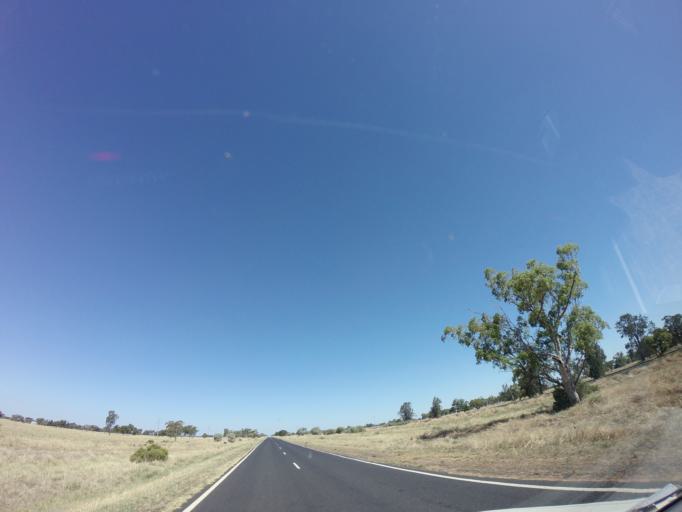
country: AU
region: New South Wales
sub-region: Bogan
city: Nyngan
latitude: -31.7035
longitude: 147.4631
